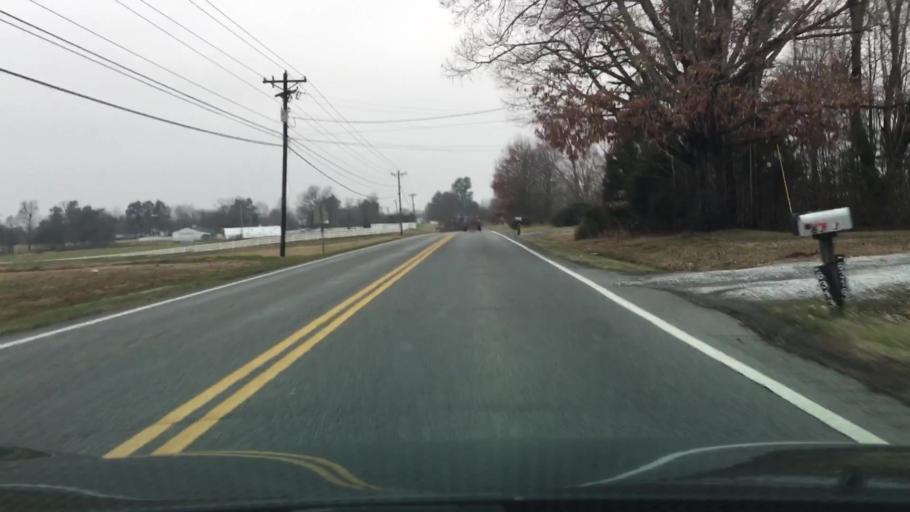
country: US
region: Kentucky
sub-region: Livingston County
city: Ledbetter
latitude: 36.9674
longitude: -88.4315
